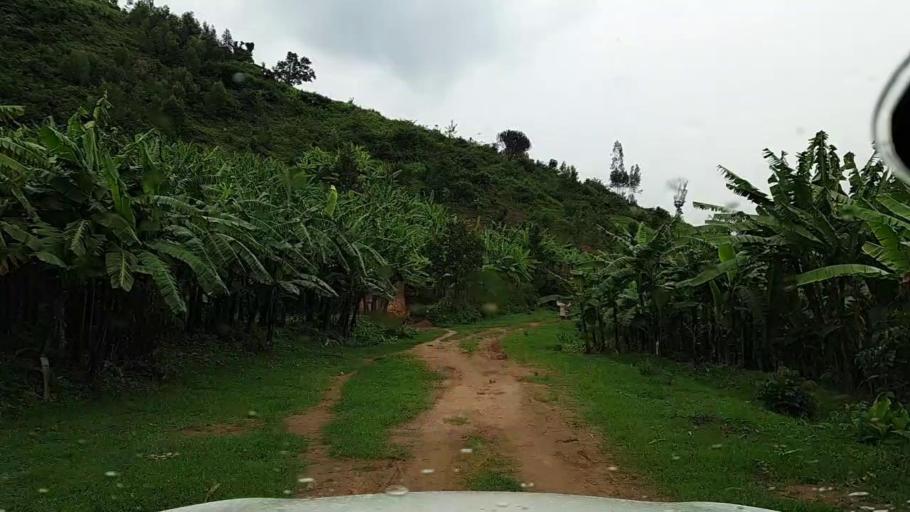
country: RW
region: Kigali
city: Kigali
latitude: -1.9087
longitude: 29.9583
